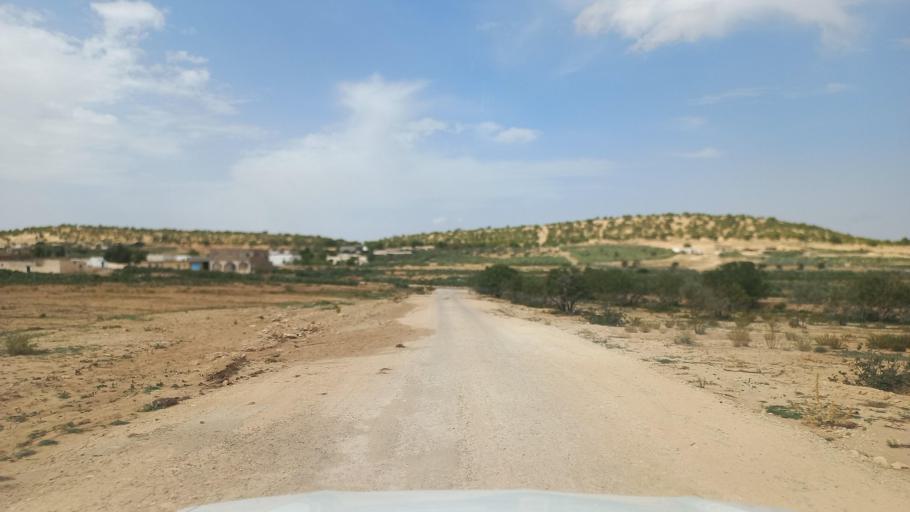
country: TN
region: Al Qasrayn
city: Kasserine
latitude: 35.3872
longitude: 8.8634
